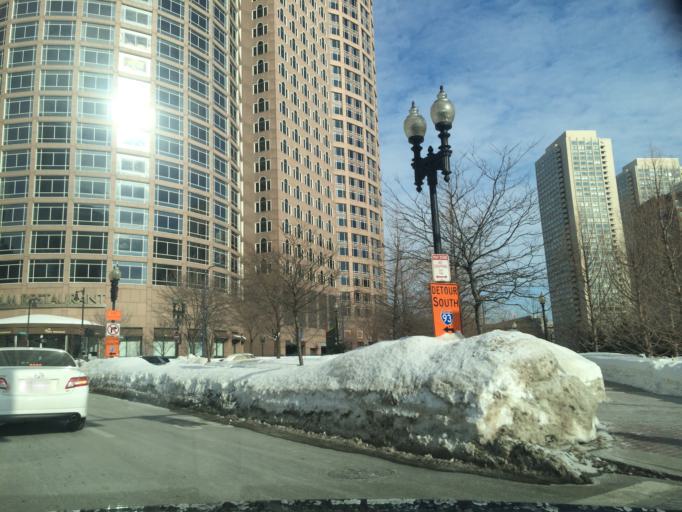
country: US
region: Massachusetts
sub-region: Suffolk County
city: Boston
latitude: 42.3549
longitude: -71.0516
